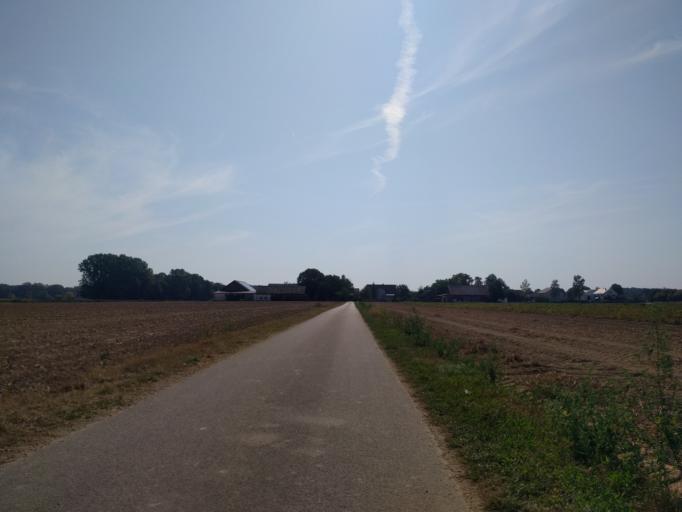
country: DE
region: Bavaria
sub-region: Upper Palatinate
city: Mintraching
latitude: 48.9886
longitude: 12.2525
